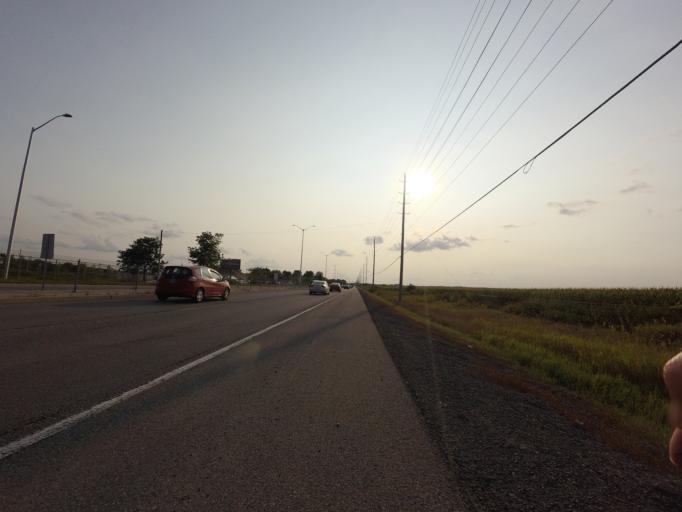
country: CA
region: Ontario
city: Bells Corners
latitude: 45.2952
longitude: -75.7403
